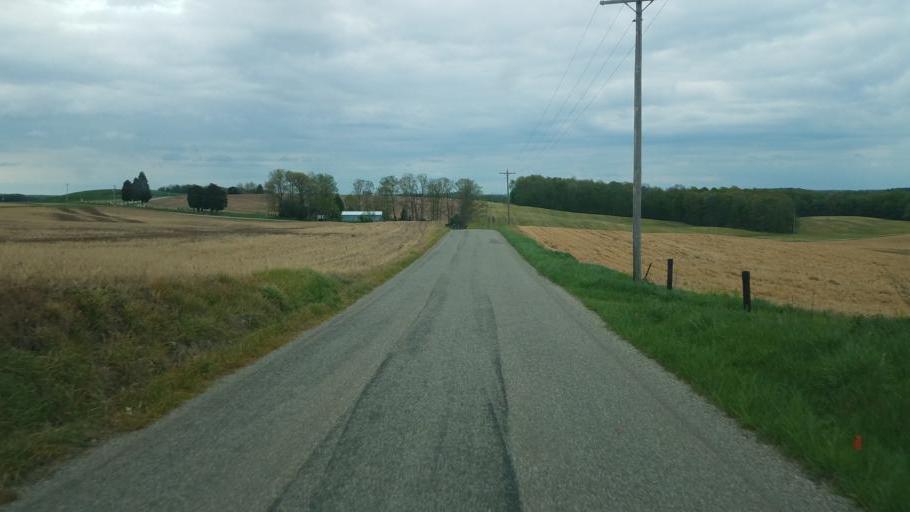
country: US
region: Ohio
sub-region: Ashland County
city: Loudonville
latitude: 40.6311
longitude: -82.3014
